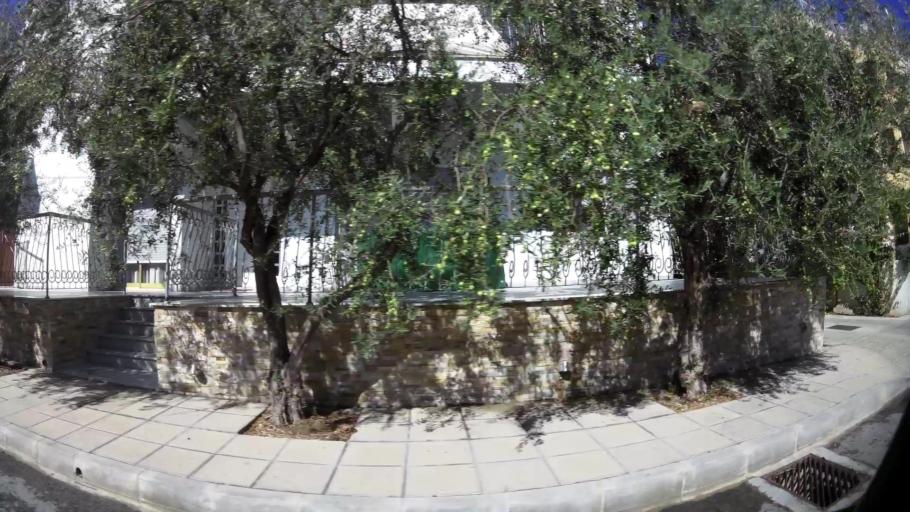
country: CY
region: Lefkosia
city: Nicosia
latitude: 35.1444
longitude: 33.3467
